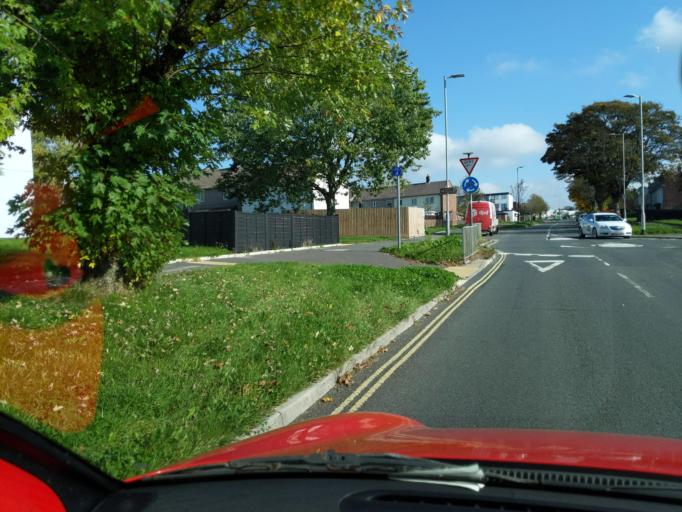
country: GB
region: England
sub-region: Plymouth
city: Plymouth
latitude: 50.4286
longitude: -4.1283
